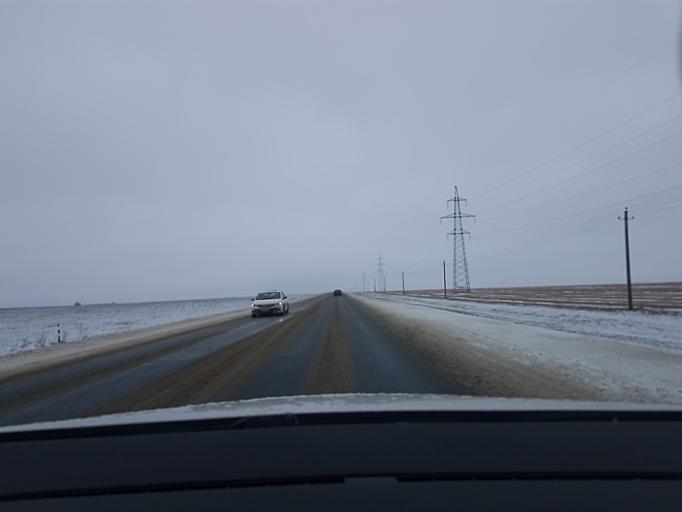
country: RU
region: Rjazan
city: Mikhaylov
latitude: 54.0951
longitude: 39.2191
